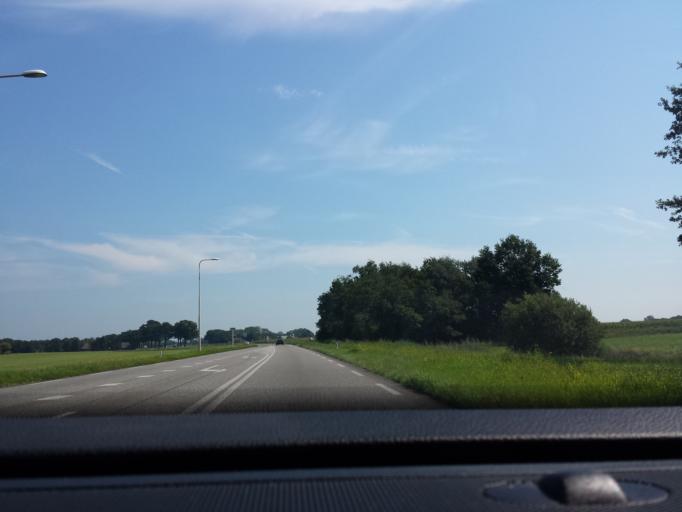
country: NL
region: Gelderland
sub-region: Gemeente Lochem
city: Lochem
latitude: 52.1659
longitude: 6.4451
